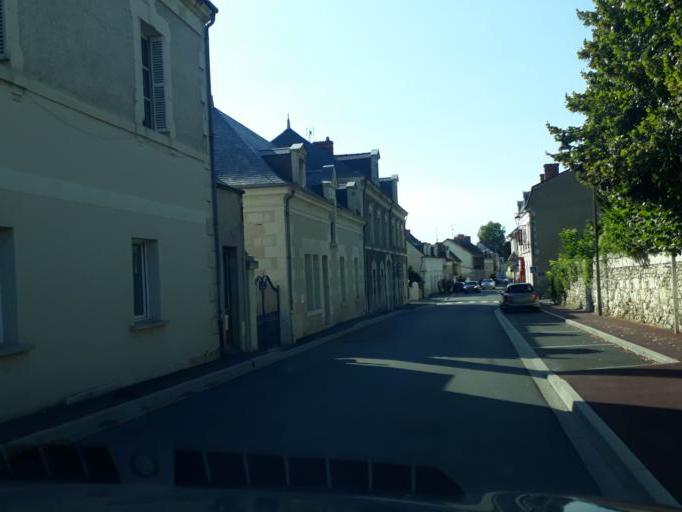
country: FR
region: Centre
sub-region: Departement du Loir-et-Cher
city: Thesee
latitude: 47.3255
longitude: 1.3053
